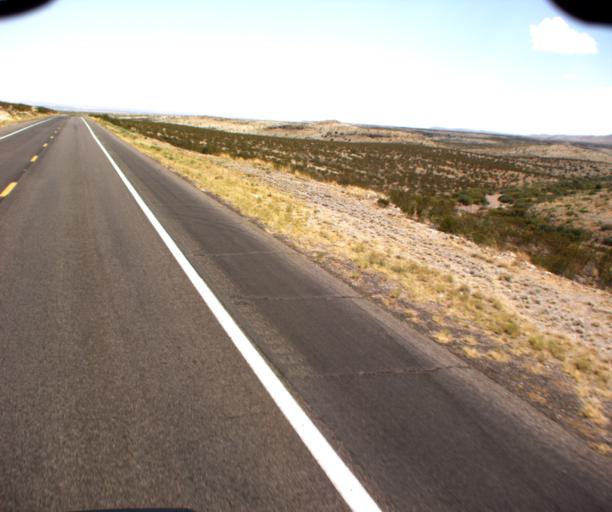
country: US
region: Arizona
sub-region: Greenlee County
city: Clifton
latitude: 32.7329
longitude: -109.1914
